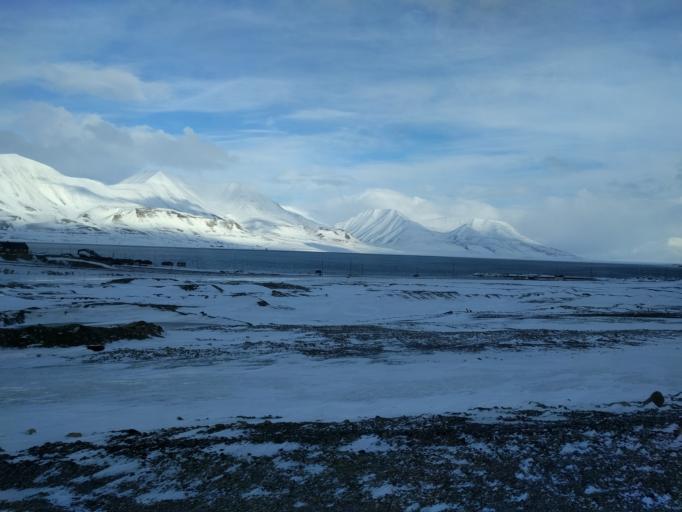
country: SJ
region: Svalbard
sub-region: Spitsbergen
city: Longyearbyen
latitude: 78.2409
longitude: 15.5182
